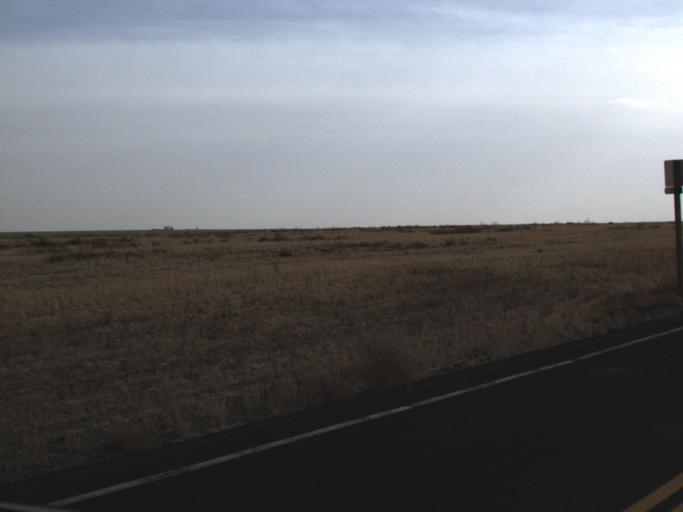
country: US
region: Washington
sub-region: Adams County
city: Ritzville
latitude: 47.3698
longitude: -118.6994
